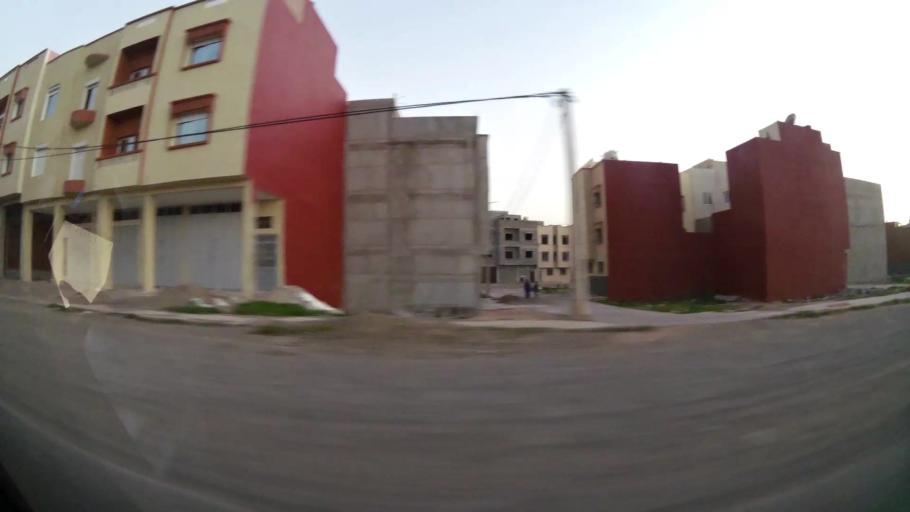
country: MA
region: Souss-Massa-Draa
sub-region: Inezgane-Ait Mellou
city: Inezgane
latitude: 30.3757
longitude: -9.4863
